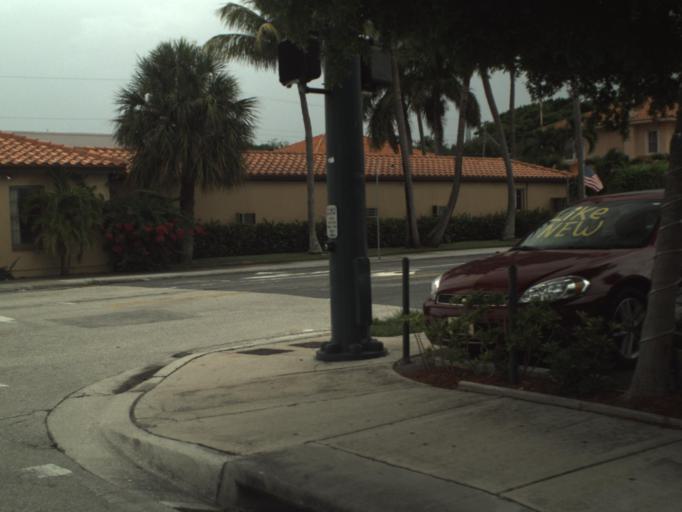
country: US
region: Florida
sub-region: Palm Beach County
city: Lake Clarke Shores
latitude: 26.6744
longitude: -80.0549
